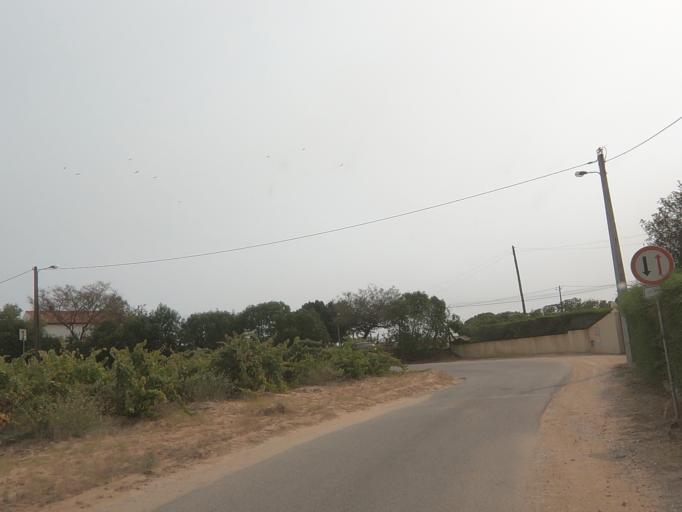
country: PT
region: Faro
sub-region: Lagoa
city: Carvoeiro
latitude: 37.1007
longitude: -8.4128
